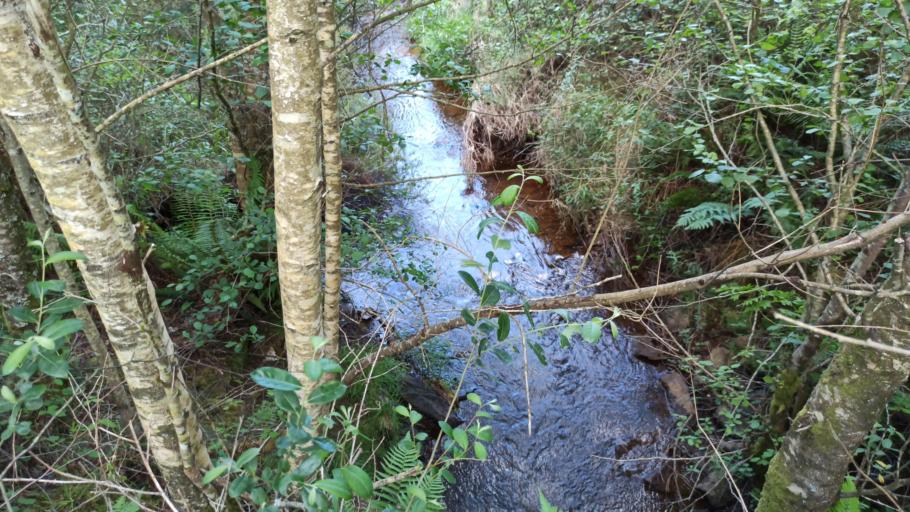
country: ES
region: Galicia
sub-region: Provincia da Coruna
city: Santa Comba
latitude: 43.0797
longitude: -8.7194
